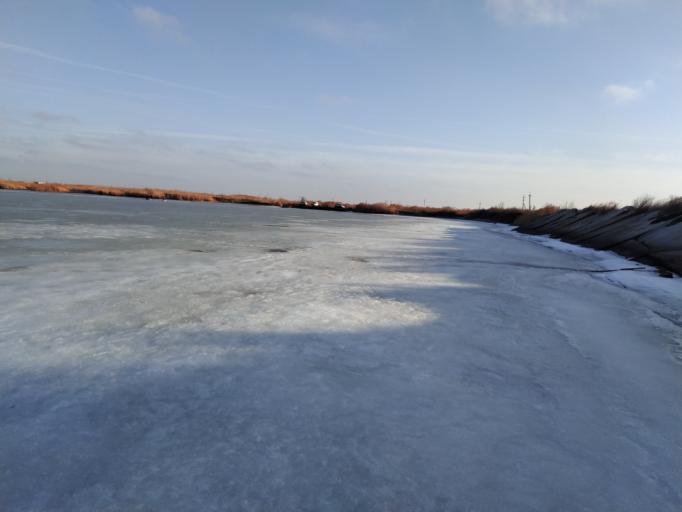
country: RU
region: Rostov
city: Bataysk
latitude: 47.1446
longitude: 39.6592
